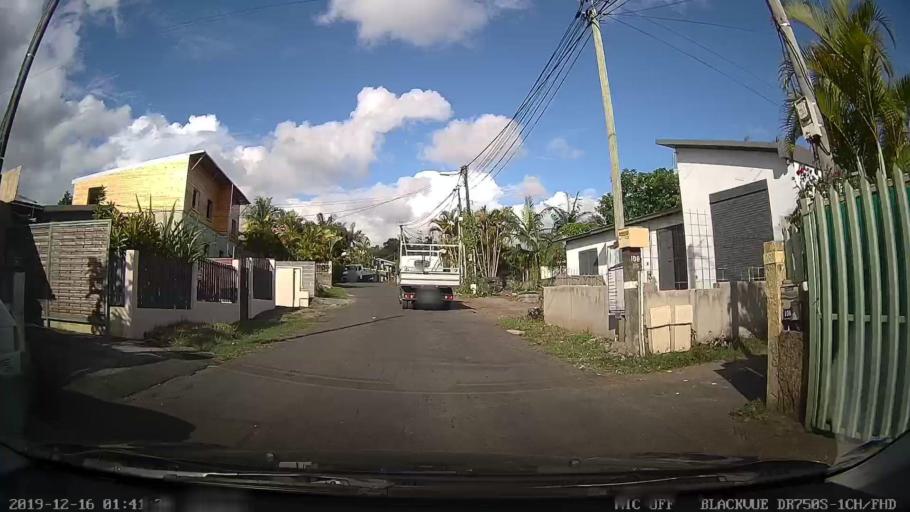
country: RE
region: Reunion
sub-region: Reunion
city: Le Tampon
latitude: -21.2556
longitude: 55.5089
